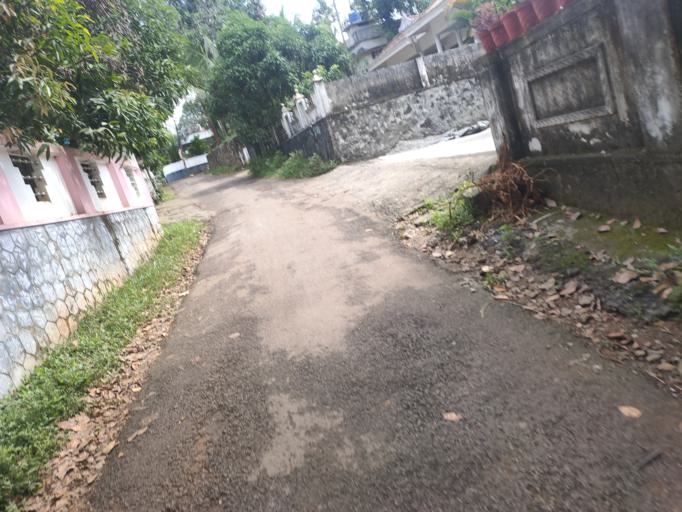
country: IN
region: Kerala
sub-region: Ernakulam
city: Kotamangalam
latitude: 10.0055
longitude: 76.6431
